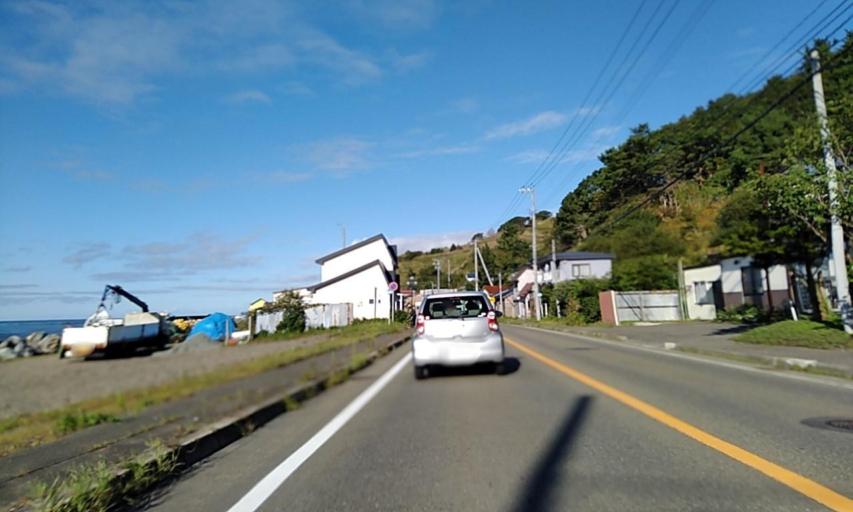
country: JP
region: Hokkaido
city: Shizunai-furukawacho
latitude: 42.1772
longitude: 142.7492
